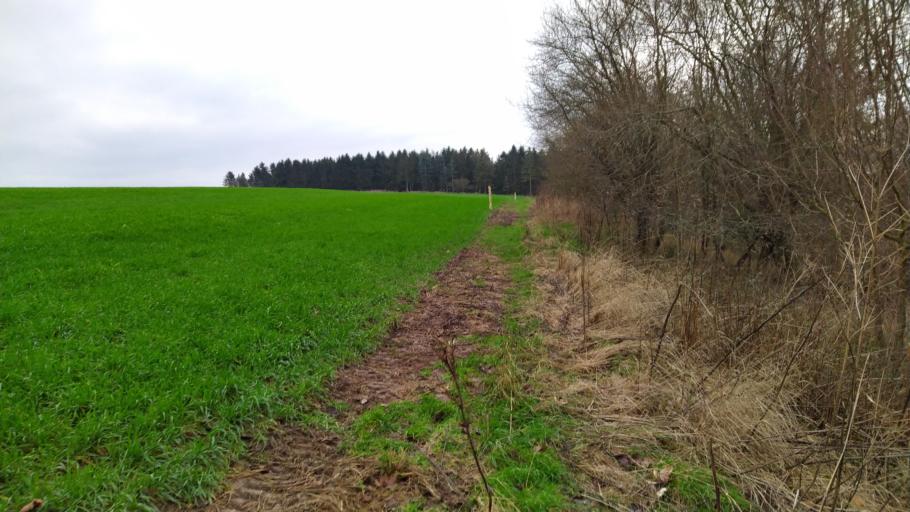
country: DK
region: Capital Region
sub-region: Egedal Kommune
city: Vekso
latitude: 55.7503
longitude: 12.2295
